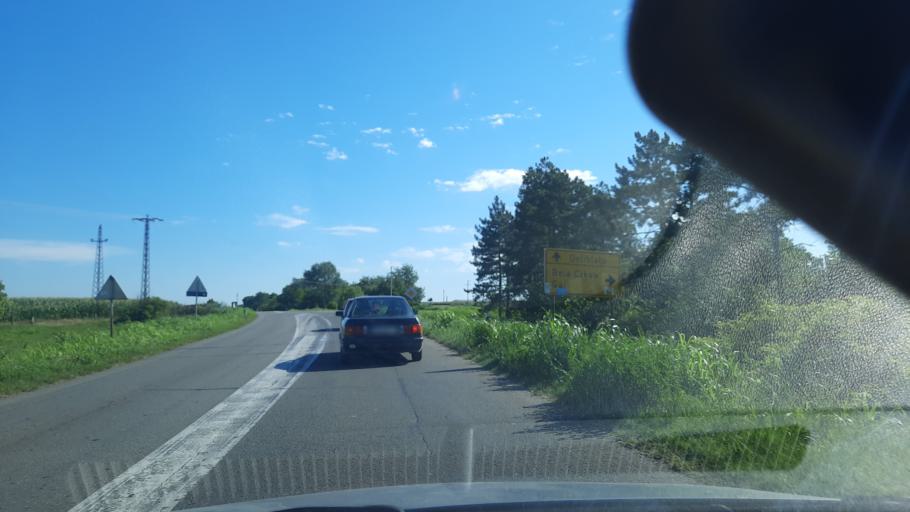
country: RS
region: Autonomna Pokrajina Vojvodina
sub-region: Juznobanatski Okrug
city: Kovin
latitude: 44.7732
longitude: 20.9997
